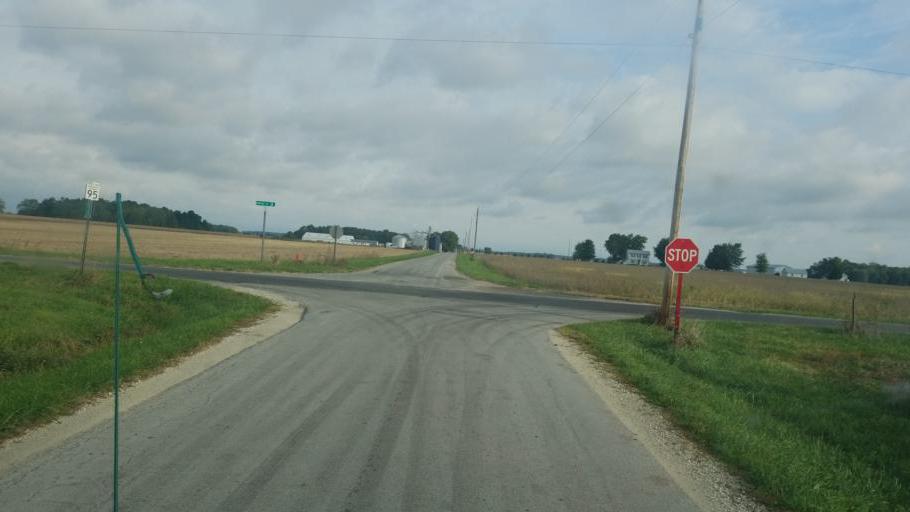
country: US
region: Ohio
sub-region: Wyandot County
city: Carey
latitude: 40.9916
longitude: -83.4298
